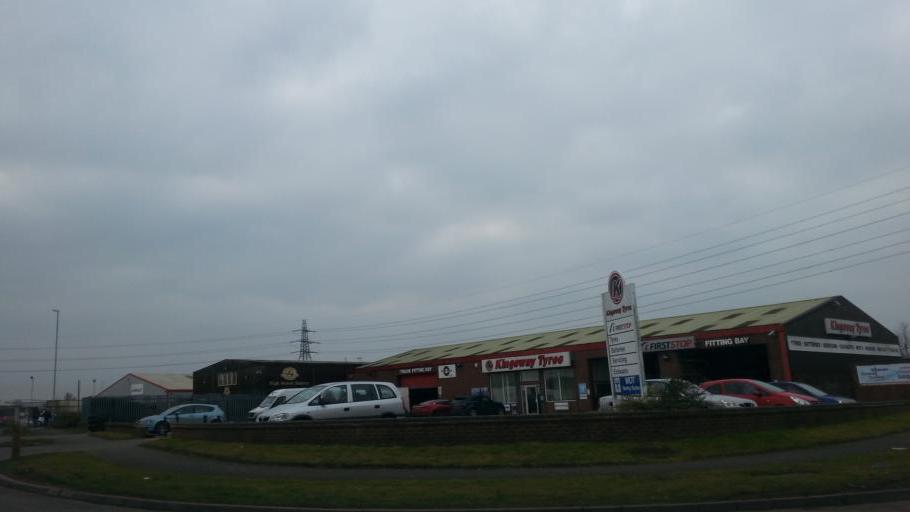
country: GB
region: England
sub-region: Northamptonshire
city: Corby
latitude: 52.4956
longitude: -0.6751
